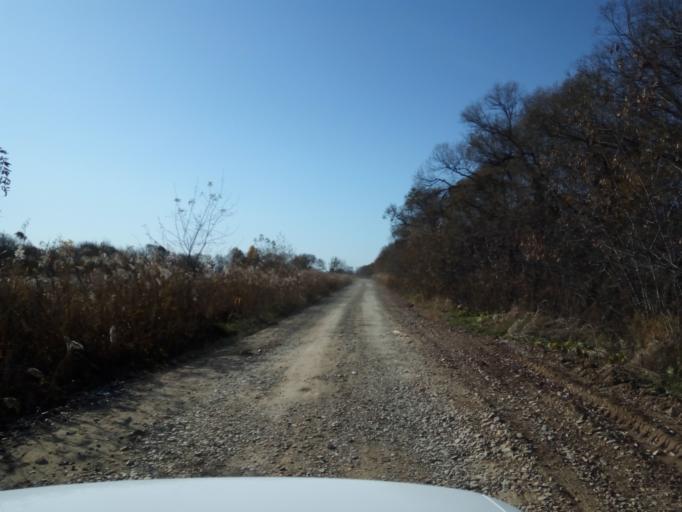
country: RU
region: Primorskiy
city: Dal'nerechensk
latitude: 45.9093
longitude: 133.7968
